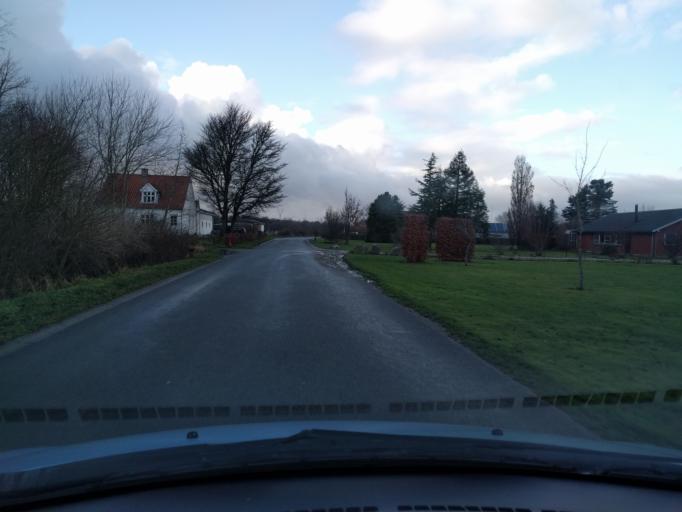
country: DK
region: South Denmark
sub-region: Kerteminde Kommune
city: Langeskov
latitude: 55.3936
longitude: 10.5619
